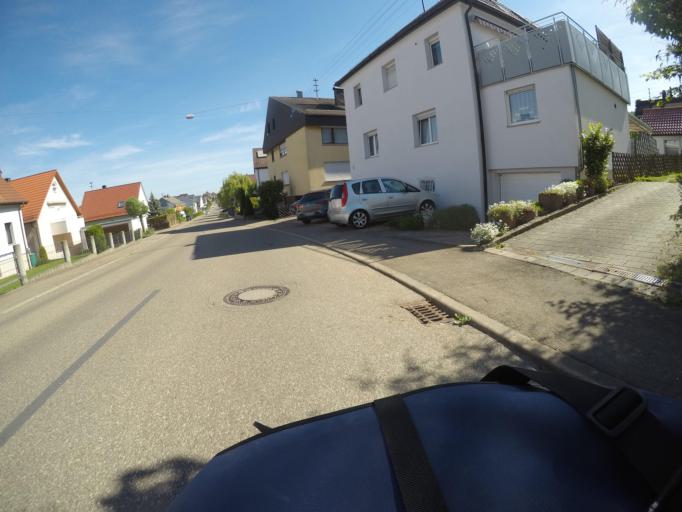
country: DE
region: Baden-Wuerttemberg
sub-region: Regierungsbezirk Stuttgart
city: Aalen
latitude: 48.8631
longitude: 10.1075
